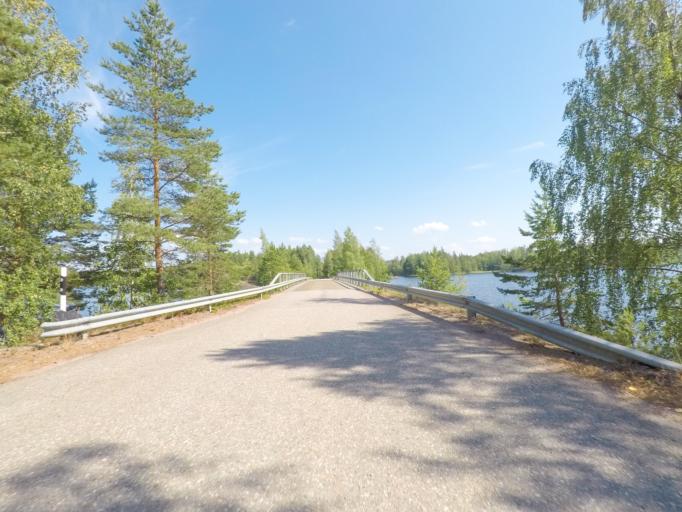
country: FI
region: Southern Savonia
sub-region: Mikkeli
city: Puumala
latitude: 61.4054
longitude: 28.0704
